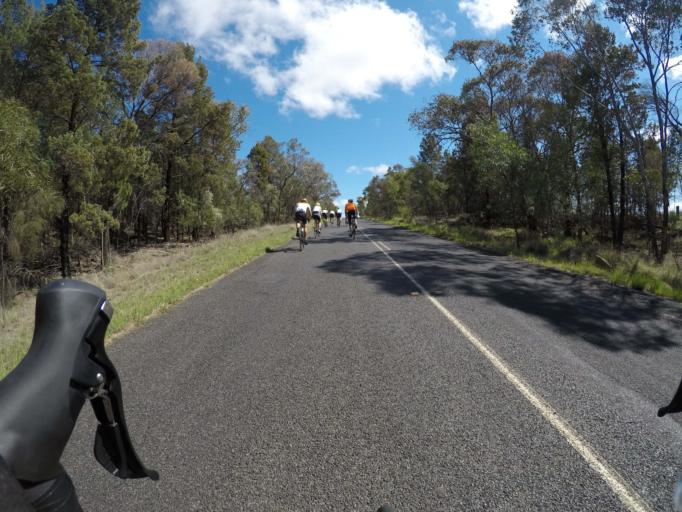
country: AU
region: New South Wales
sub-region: Dubbo Municipality
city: Eulomogo
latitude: -32.6036
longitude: 148.5458
